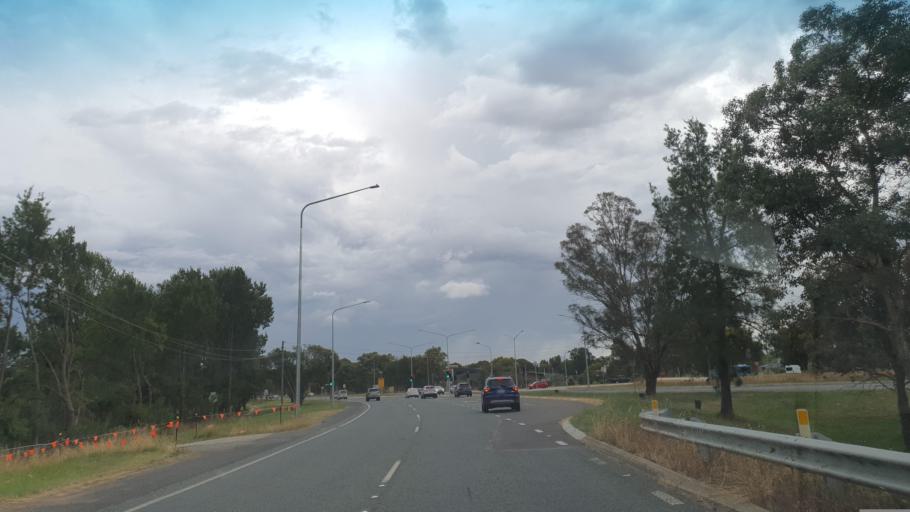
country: AU
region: Australian Capital Territory
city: Belconnen
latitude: -35.2082
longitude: 149.0354
